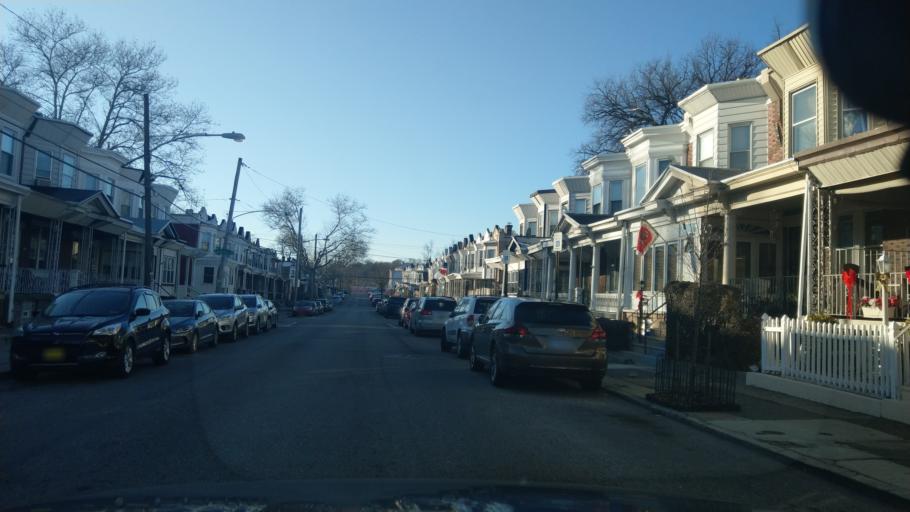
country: US
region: Pennsylvania
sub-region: Montgomery County
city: Wyncote
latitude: 40.0505
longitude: -75.1540
